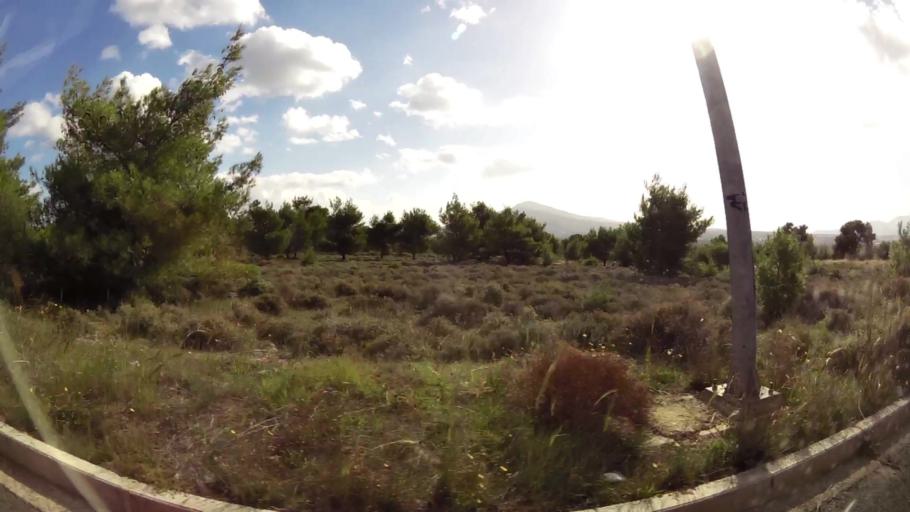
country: GR
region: Attica
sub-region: Nomarchia Anatolikis Attikis
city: Thrakomakedones
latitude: 38.1261
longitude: 23.7673
